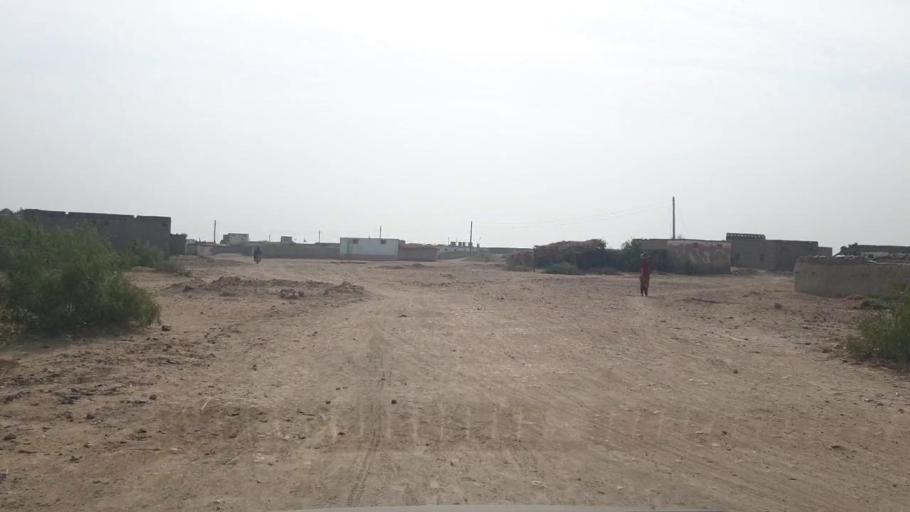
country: PK
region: Sindh
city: Tando Muhammad Khan
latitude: 25.1586
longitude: 68.4708
